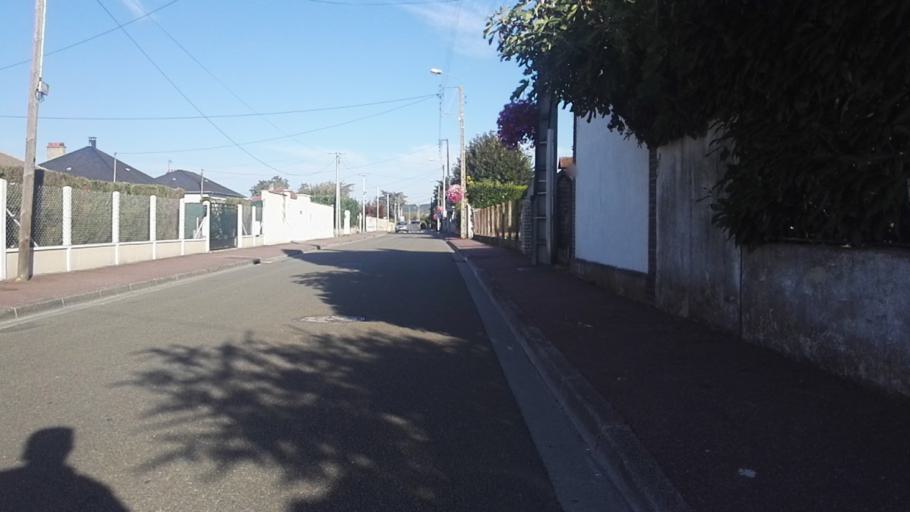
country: FR
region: Haute-Normandie
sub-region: Departement de l'Eure
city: Pacy-sur-Eure
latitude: 49.0198
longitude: 1.3757
